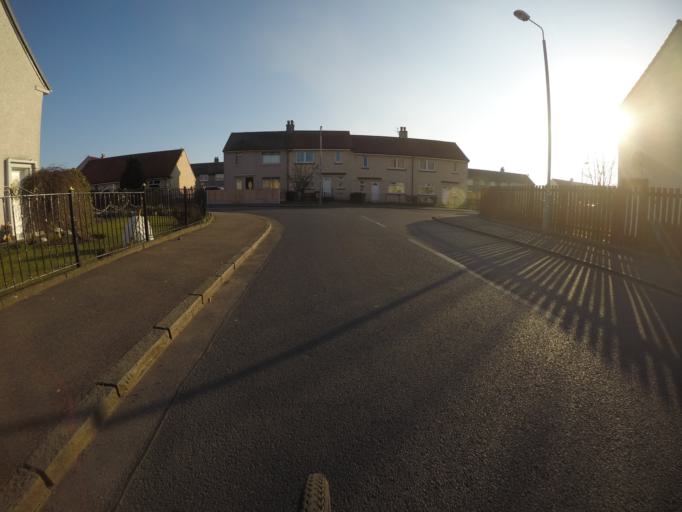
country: GB
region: Scotland
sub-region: North Ayrshire
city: Kilwinning
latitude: 55.6494
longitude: -4.7020
